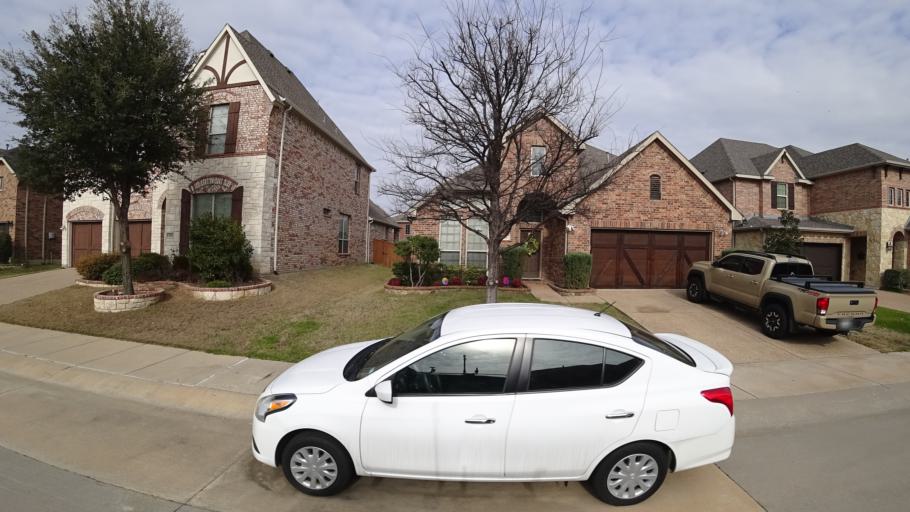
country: US
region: Texas
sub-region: Denton County
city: The Colony
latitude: 33.0521
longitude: -96.9057
